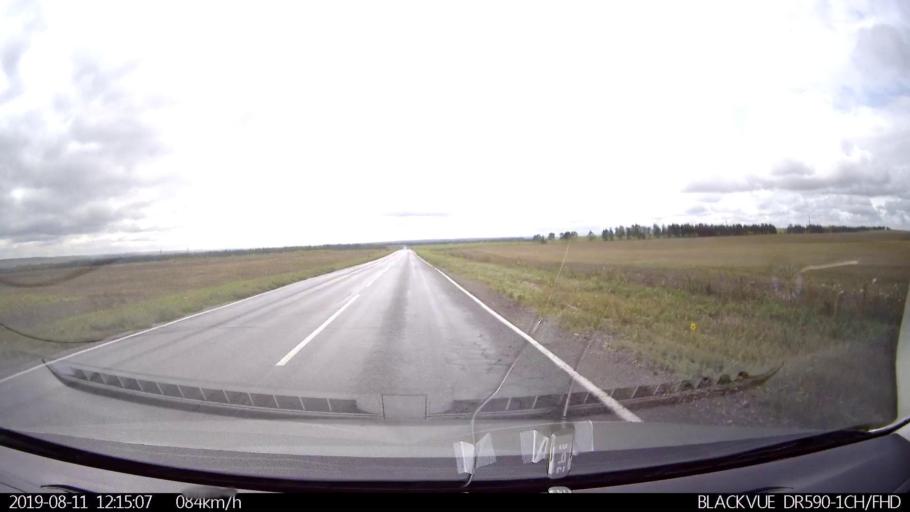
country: RU
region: Ulyanovsk
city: Ignatovka
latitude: 53.9451
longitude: 47.9714
